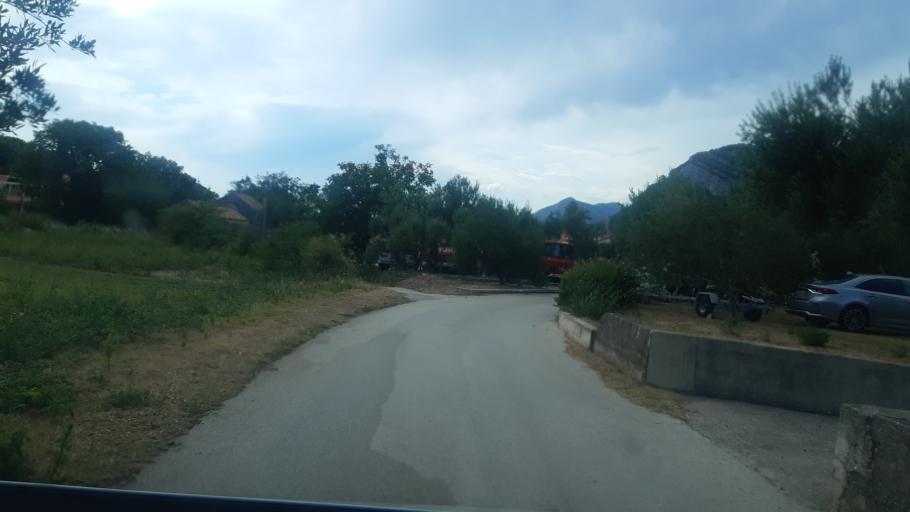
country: HR
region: Dubrovacko-Neretvanska
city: Blato
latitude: 42.8910
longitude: 17.4567
